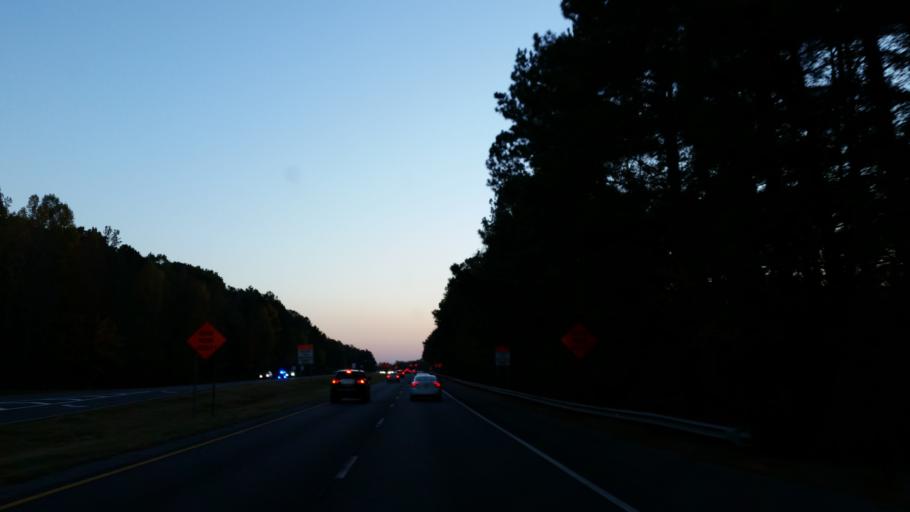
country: US
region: Georgia
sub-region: Forsyth County
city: Cumming
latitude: 34.2676
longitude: -84.0830
